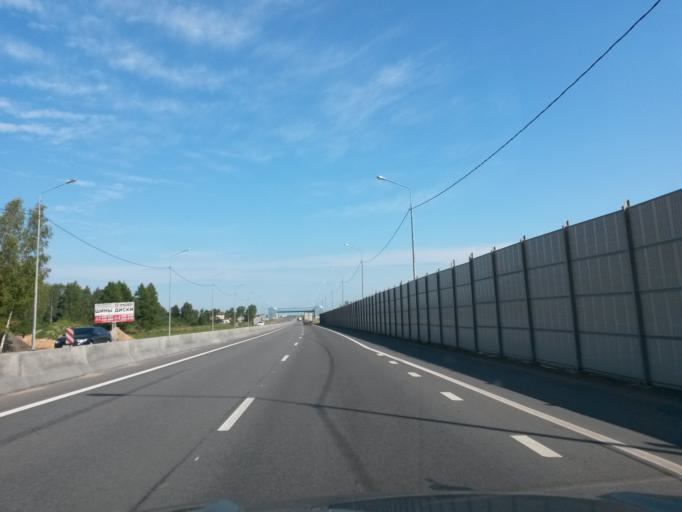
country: RU
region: Jaroslavl
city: Yaroslavl
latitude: 57.7129
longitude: 39.9036
